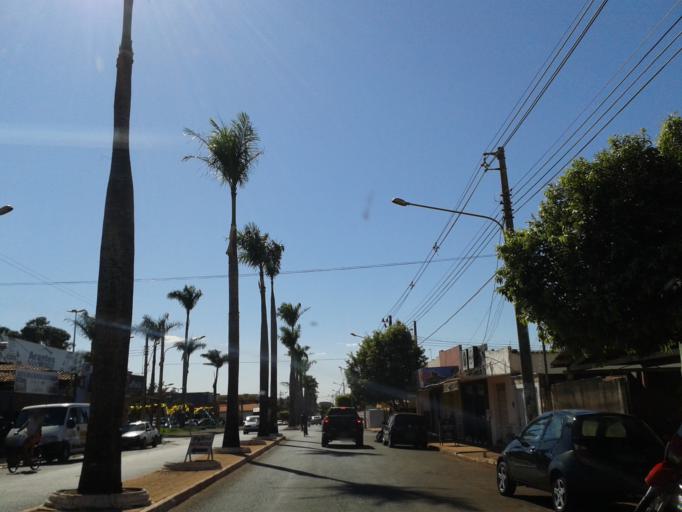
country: BR
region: Minas Gerais
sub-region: Centralina
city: Centralina
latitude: -18.5849
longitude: -49.1980
